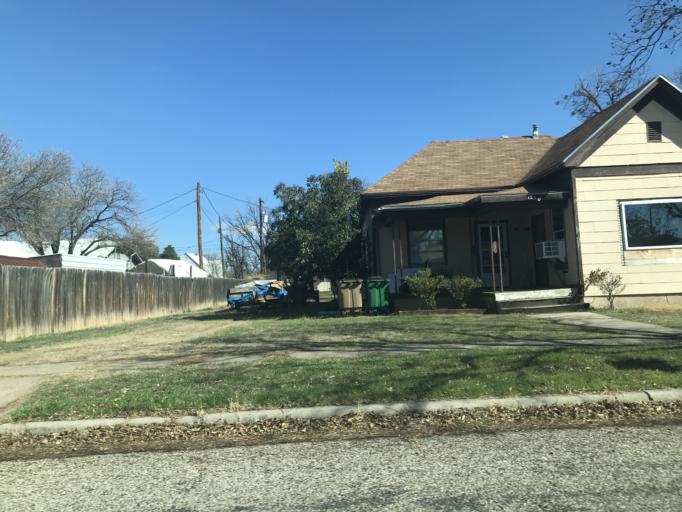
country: US
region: Texas
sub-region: Tom Green County
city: San Angelo
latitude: 31.4493
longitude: -100.4446
